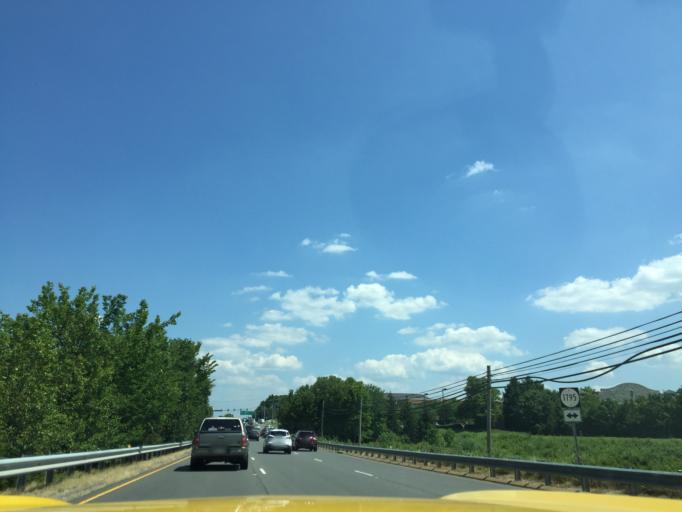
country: US
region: Virginia
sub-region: Loudoun County
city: Dulles Town Center
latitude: 39.0349
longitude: -77.4107
